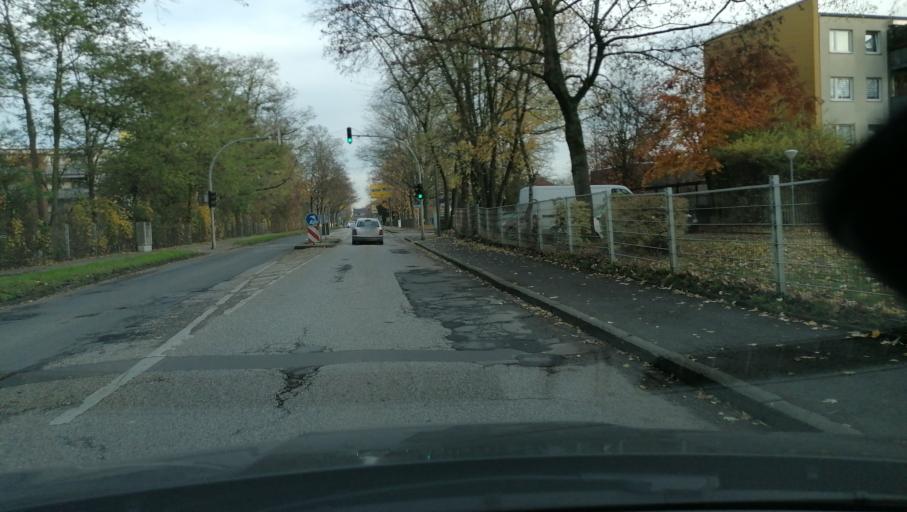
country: DE
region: North Rhine-Westphalia
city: Waltrop
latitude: 51.5727
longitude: 7.3737
